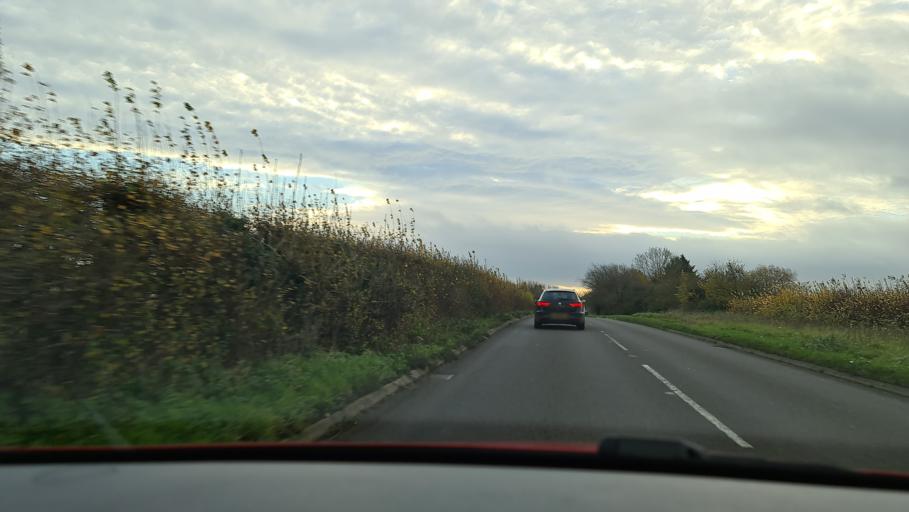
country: GB
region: England
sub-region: Oxfordshire
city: Bicester
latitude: 51.8719
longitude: -1.1062
